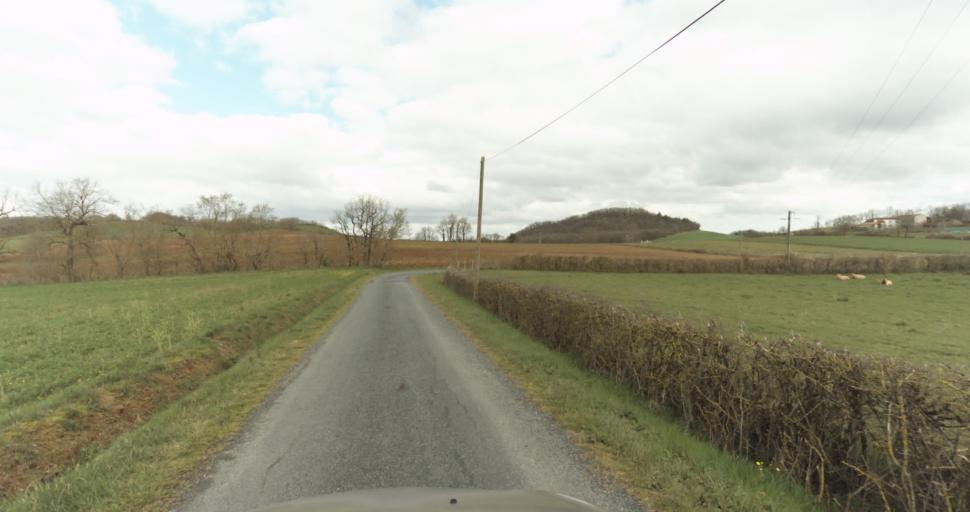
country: FR
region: Midi-Pyrenees
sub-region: Departement du Tarn
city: Frejairolles
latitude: 43.8624
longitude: 2.2187
